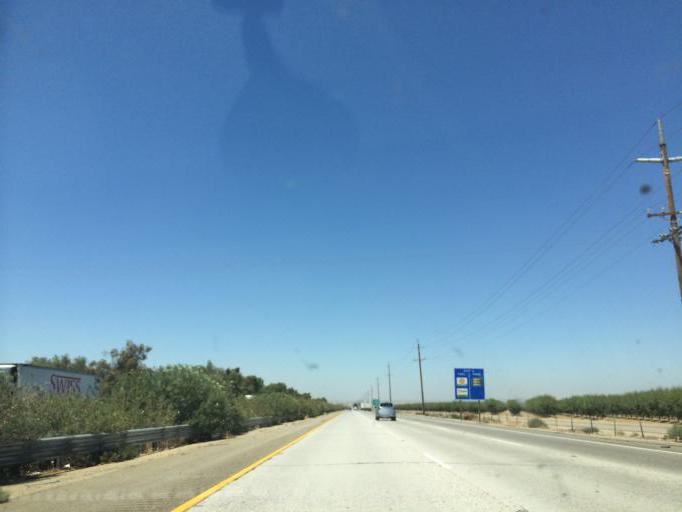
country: US
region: California
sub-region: Kern County
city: Weedpatch
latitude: 35.0409
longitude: -118.9625
